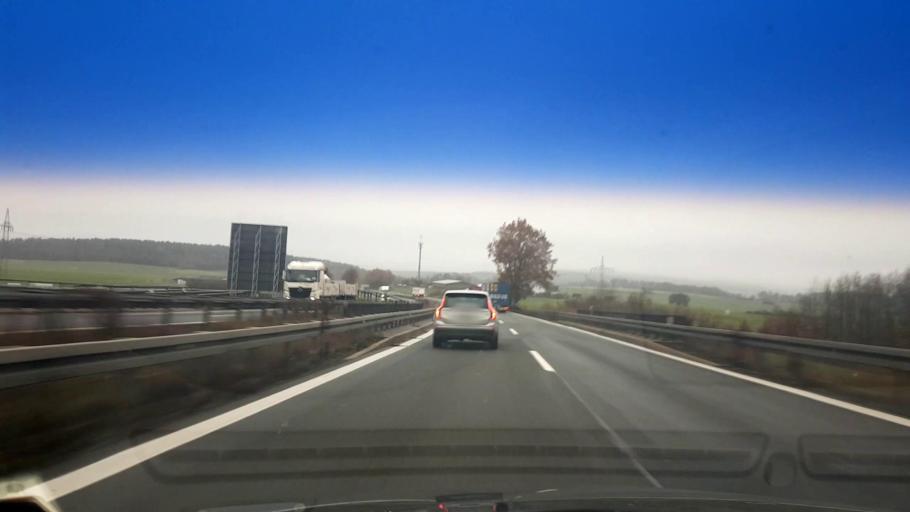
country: DE
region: Bavaria
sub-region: Upper Franconia
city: Neudrossenfeld
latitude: 50.0386
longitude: 11.4809
